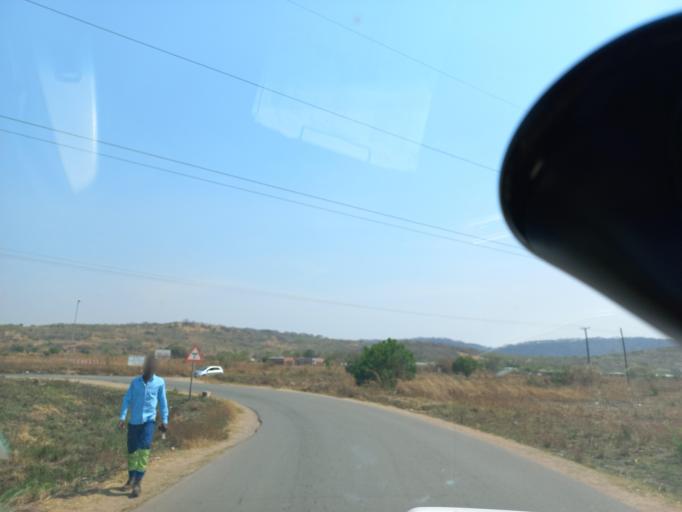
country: ZM
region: Lusaka
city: Kafue
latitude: -15.7406
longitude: 28.1737
